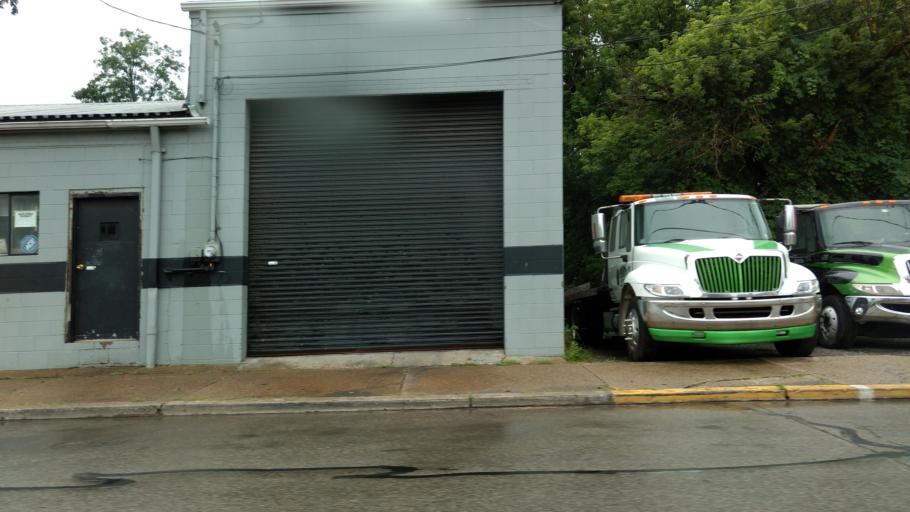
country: US
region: Pennsylvania
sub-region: Allegheny County
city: Coraopolis
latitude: 40.5156
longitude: -80.1562
